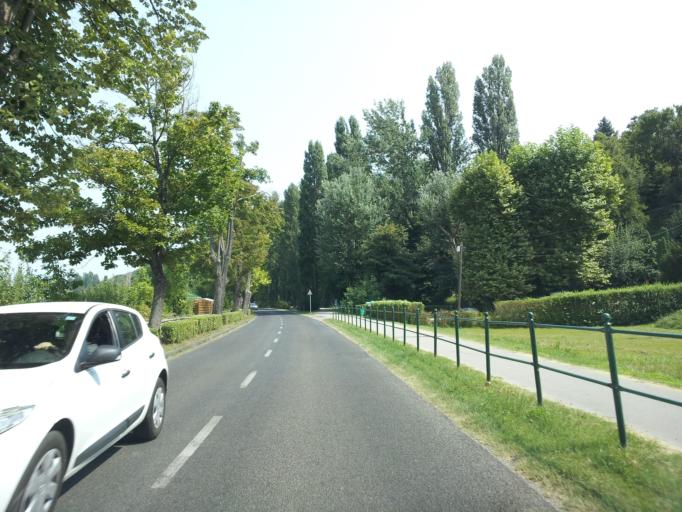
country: HU
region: Veszprem
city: Tihany
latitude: 46.9247
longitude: 17.8667
